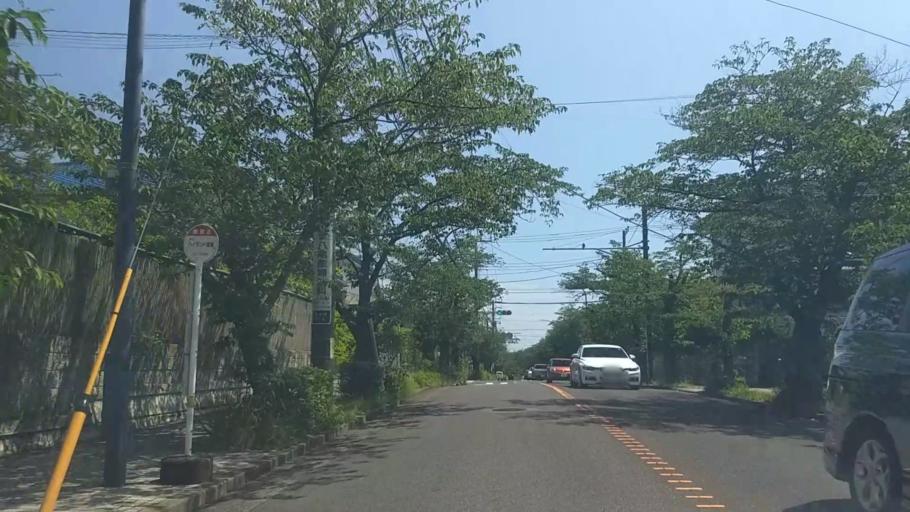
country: JP
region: Kanagawa
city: Zushi
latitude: 35.3145
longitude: 139.5769
